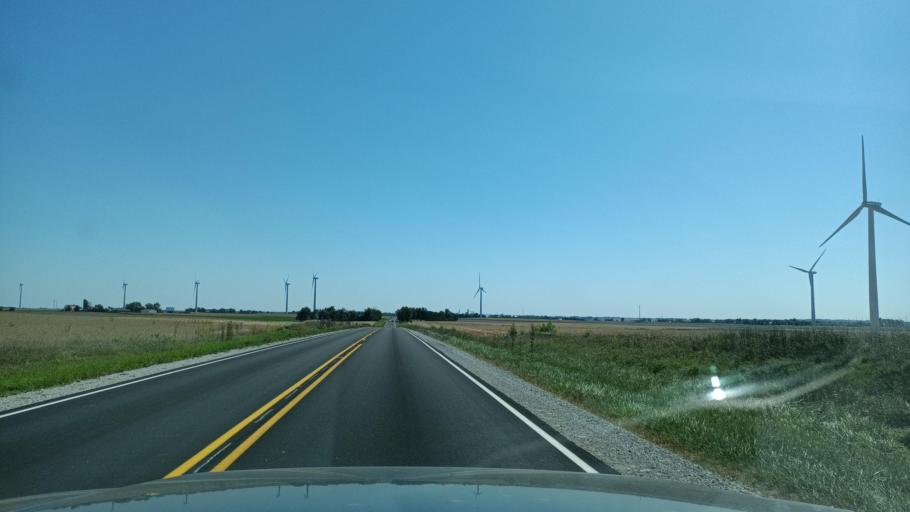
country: US
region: Illinois
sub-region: McLean County
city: Twin Grove
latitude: 40.5666
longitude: -89.0869
